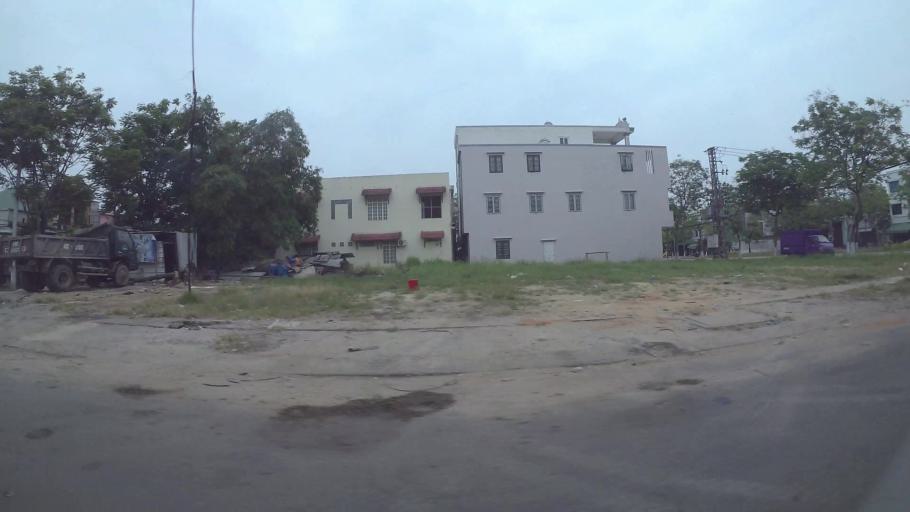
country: VN
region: Da Nang
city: Thanh Khe
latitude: 16.0542
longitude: 108.1767
